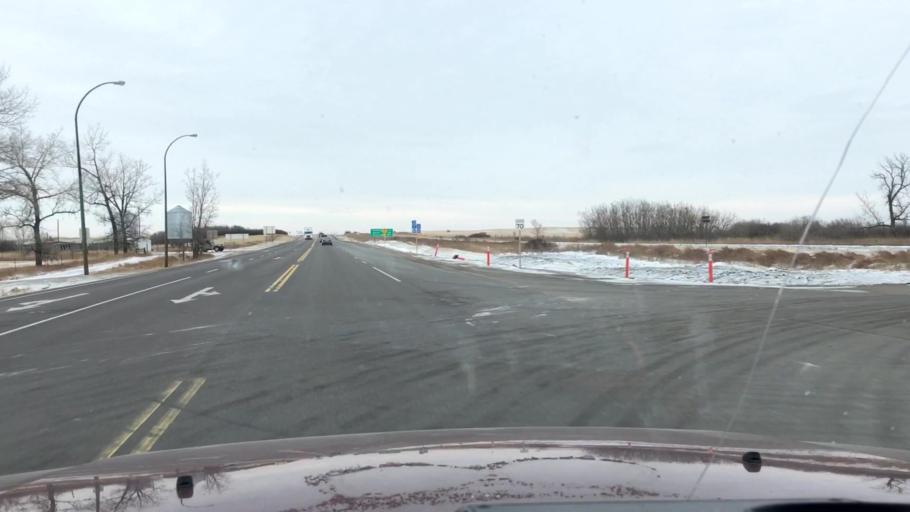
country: CA
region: Saskatchewan
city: Moose Jaw
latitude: 50.8488
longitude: -105.5633
